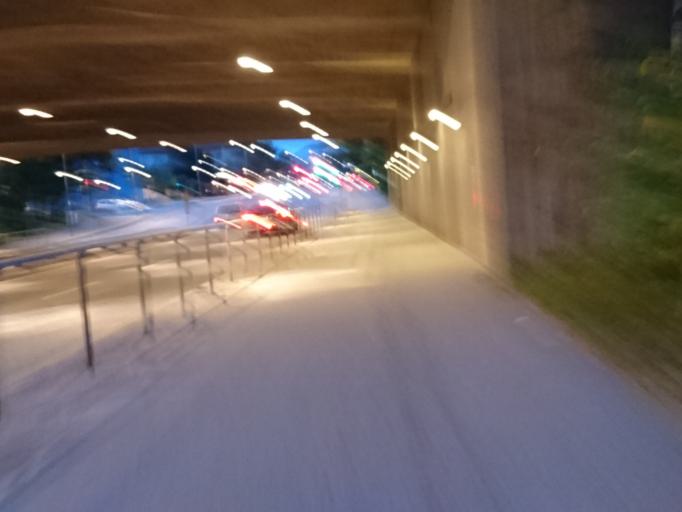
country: SE
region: Stockholm
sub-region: Stockholms Kommun
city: Arsta
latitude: 59.2769
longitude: 18.0085
